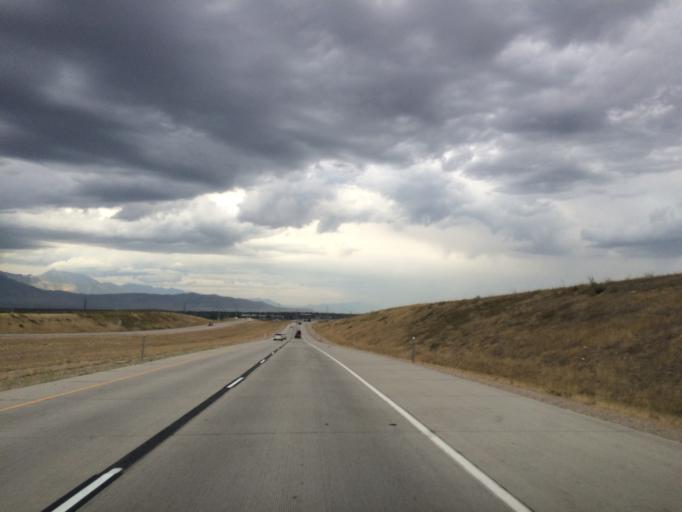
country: US
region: Utah
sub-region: Salt Lake County
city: Oquirrh
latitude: 40.6175
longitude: -112.0417
